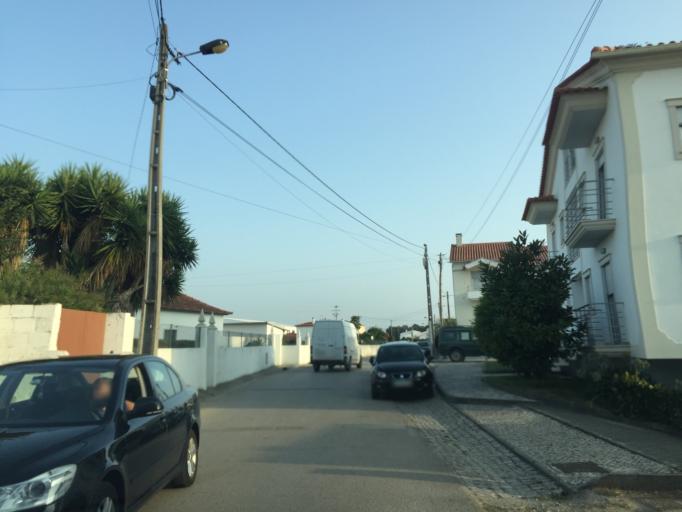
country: PT
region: Leiria
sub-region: Batalha
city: Batalha
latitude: 39.6637
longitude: -8.8329
